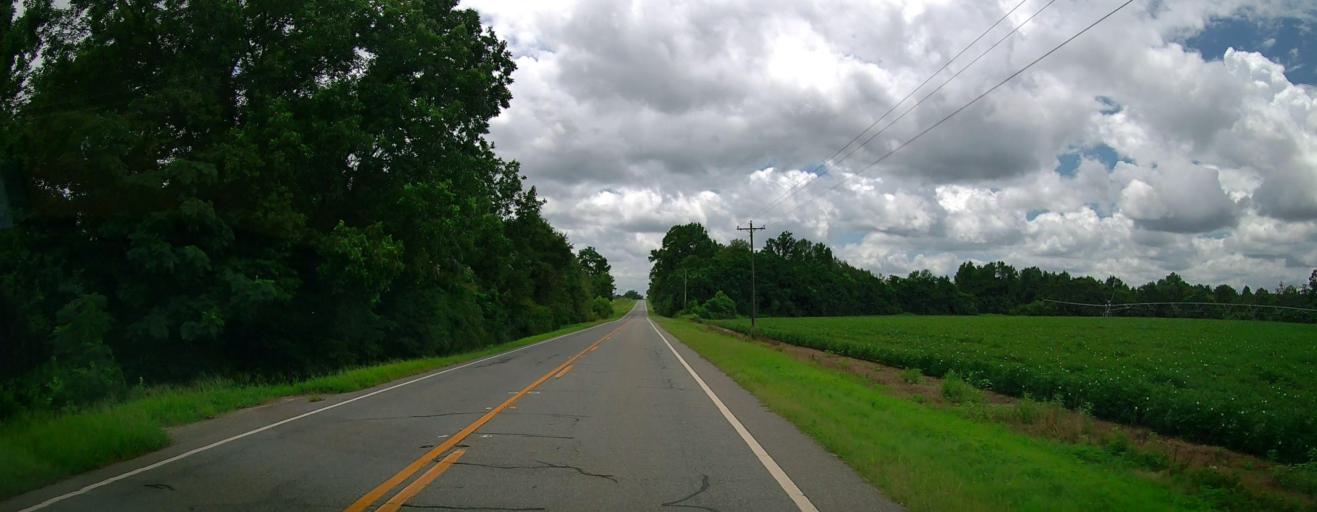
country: US
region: Georgia
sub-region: Wilcox County
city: Rochelle
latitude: 32.0177
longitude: -83.5573
